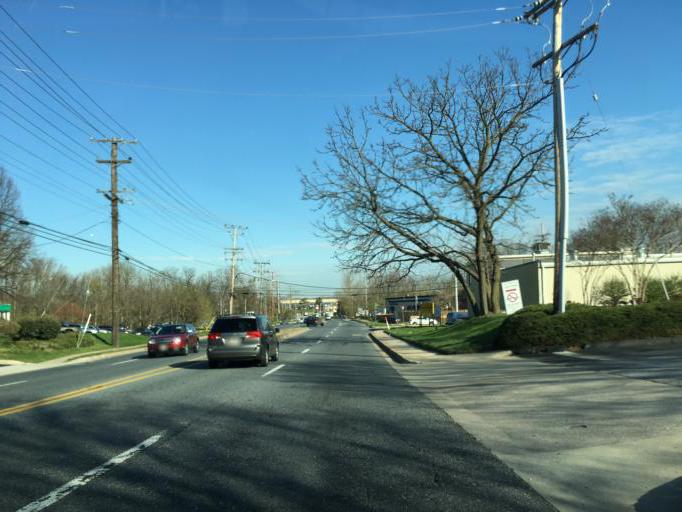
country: US
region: Maryland
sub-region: Baltimore County
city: Cockeysville
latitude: 39.4780
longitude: -76.6532
